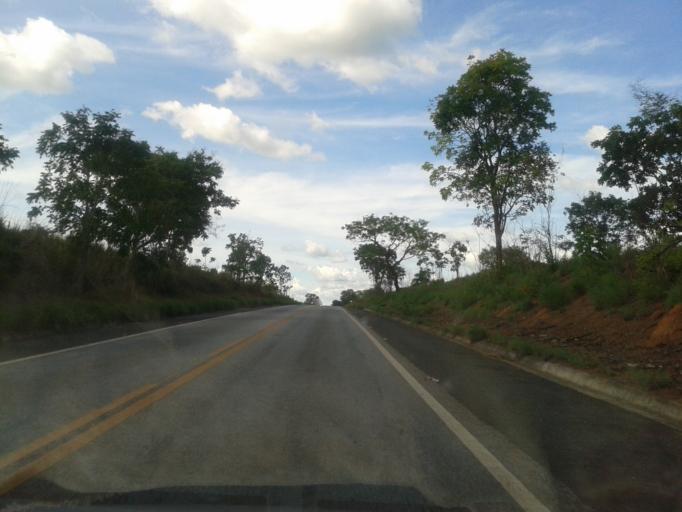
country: BR
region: Goias
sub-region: Mozarlandia
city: Mozarlandia
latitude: -14.9715
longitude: -50.5803
